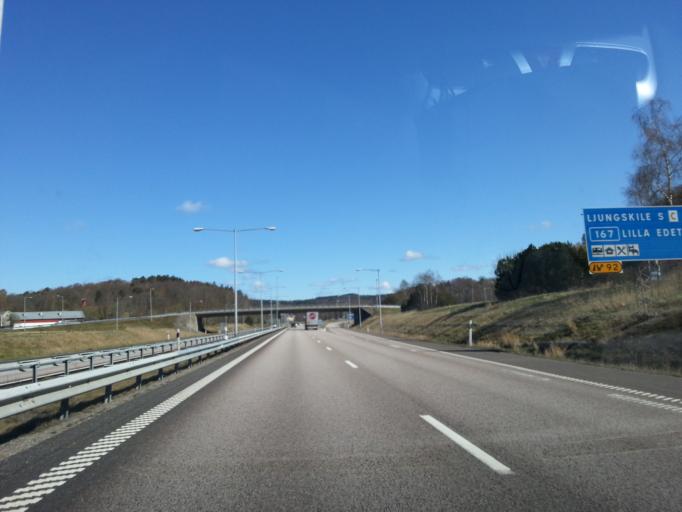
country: SE
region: Vaestra Goetaland
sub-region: Uddevalla Kommun
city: Ljungskile
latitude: 58.2115
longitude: 11.9137
